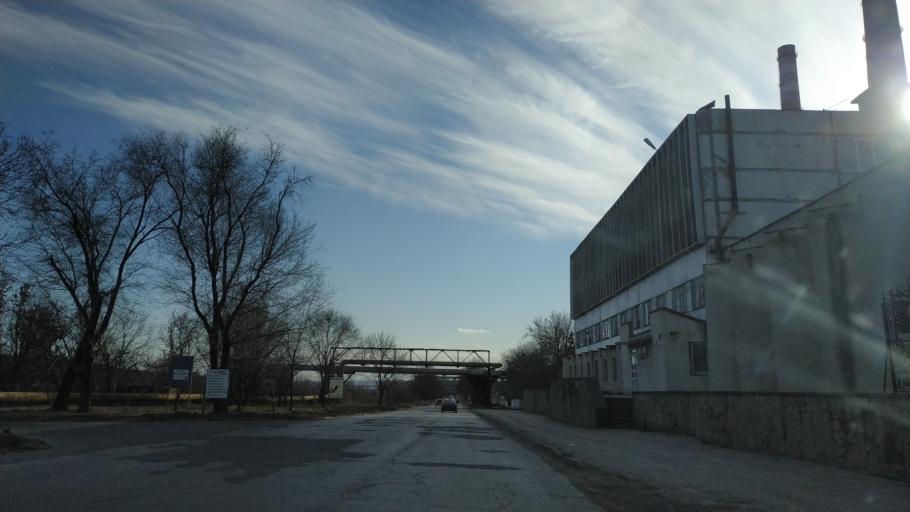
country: MD
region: Chisinau
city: Chisinau
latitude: 47.0318
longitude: 28.8968
